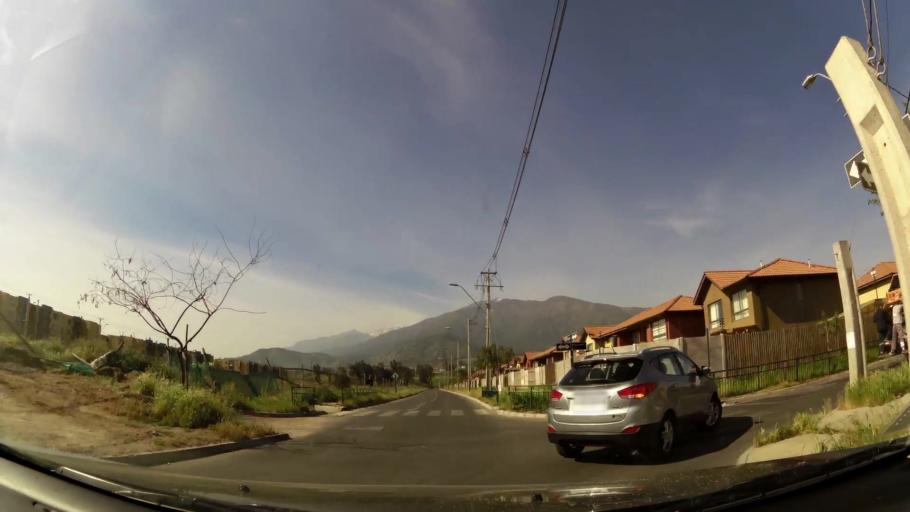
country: CL
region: Santiago Metropolitan
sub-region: Provincia de Cordillera
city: Puente Alto
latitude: -33.5893
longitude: -70.5498
